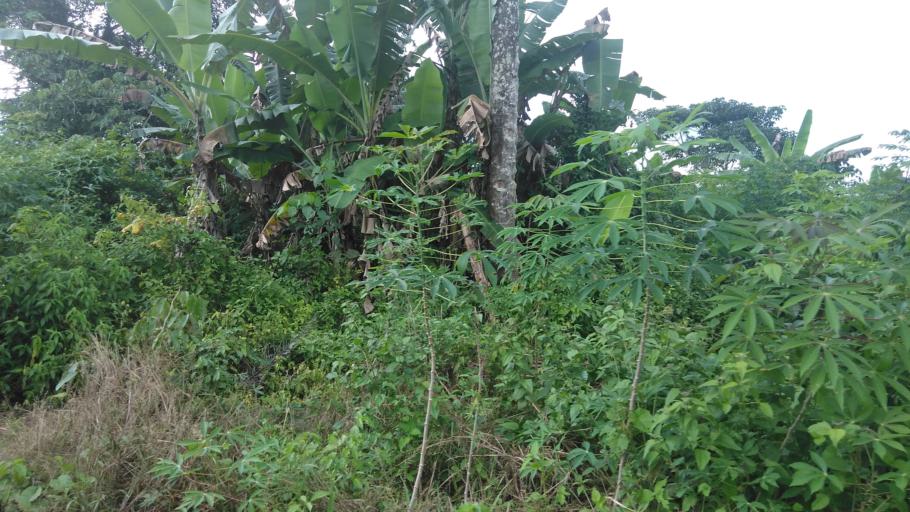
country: NG
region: Edo
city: Siluko
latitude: 6.1418
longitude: 5.2022
